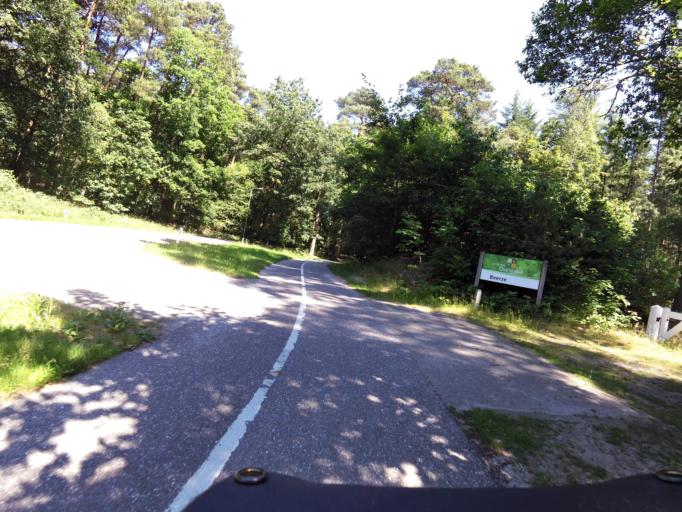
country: NL
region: Overijssel
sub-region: Gemeente Twenterand
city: Magele
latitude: 52.5082
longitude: 6.5143
